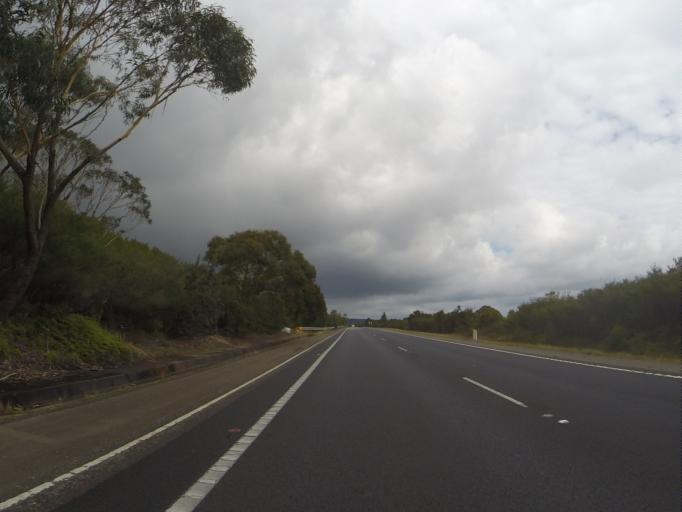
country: AU
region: New South Wales
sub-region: Wollongong
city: Bulli
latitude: -34.2595
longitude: 150.9305
